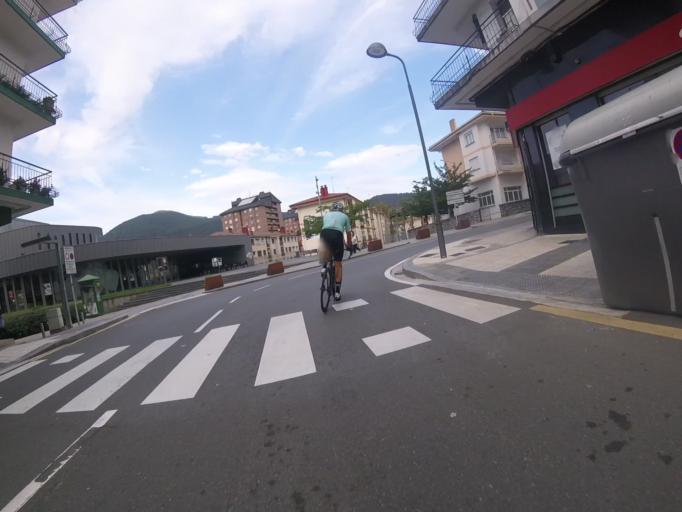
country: ES
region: Basque Country
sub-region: Provincia de Guipuzcoa
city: Andoain
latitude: 43.2179
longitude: -2.0207
